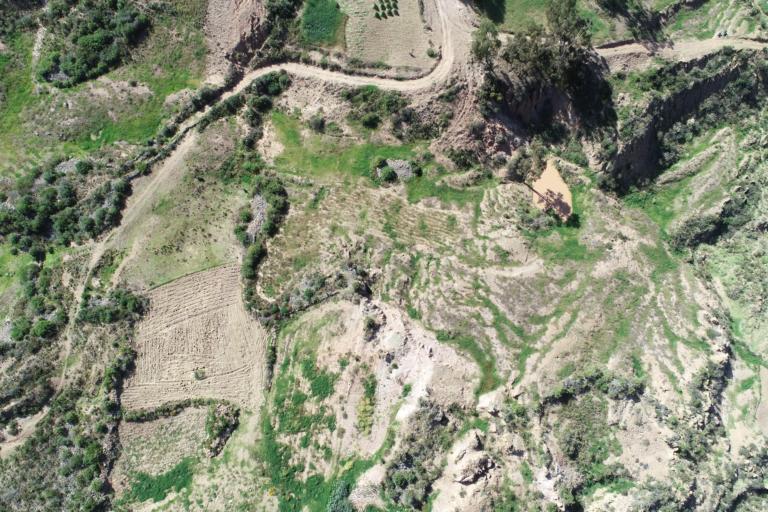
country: BO
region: La Paz
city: La Paz
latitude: -16.5577
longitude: -67.9871
